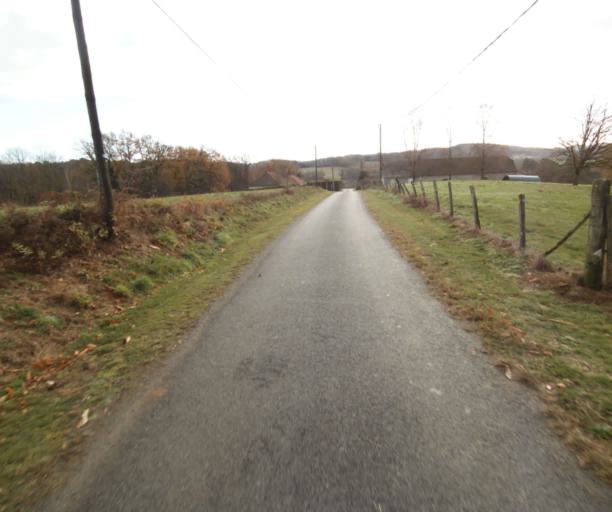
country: FR
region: Limousin
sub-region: Departement de la Correze
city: Saint-Mexant
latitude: 45.2537
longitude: 1.6360
